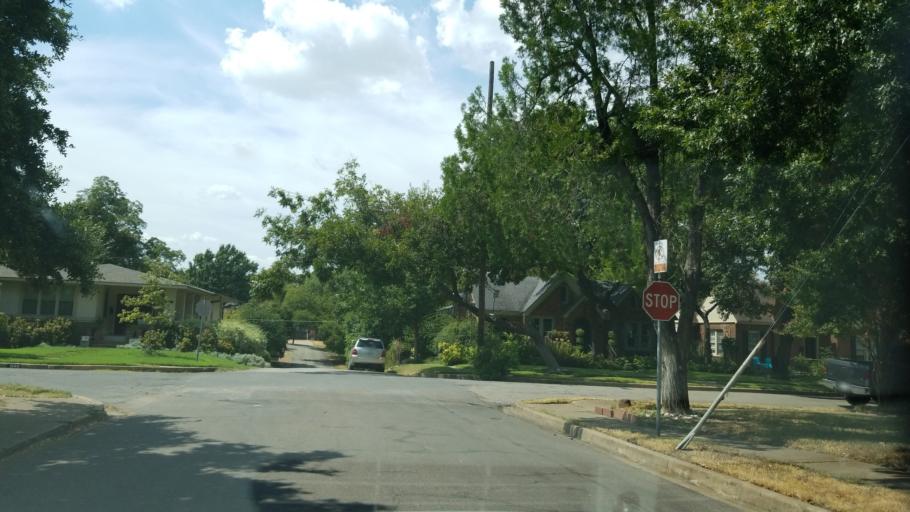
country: US
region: Texas
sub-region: Dallas County
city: Dallas
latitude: 32.7554
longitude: -96.8437
